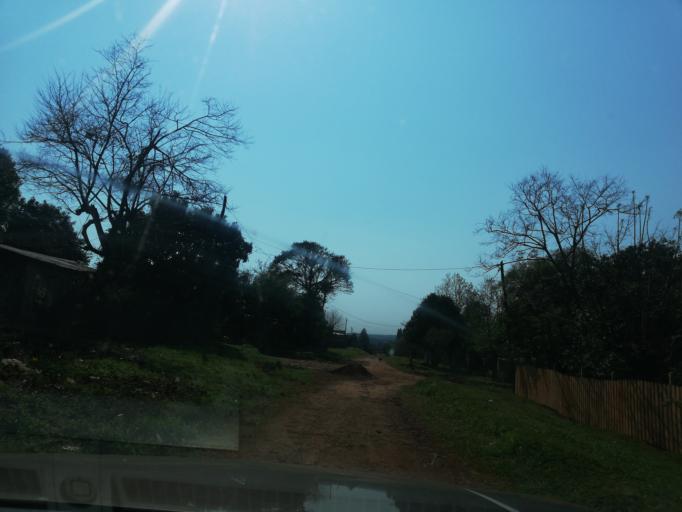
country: AR
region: Misiones
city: Bonpland
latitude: -27.4815
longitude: -55.4812
